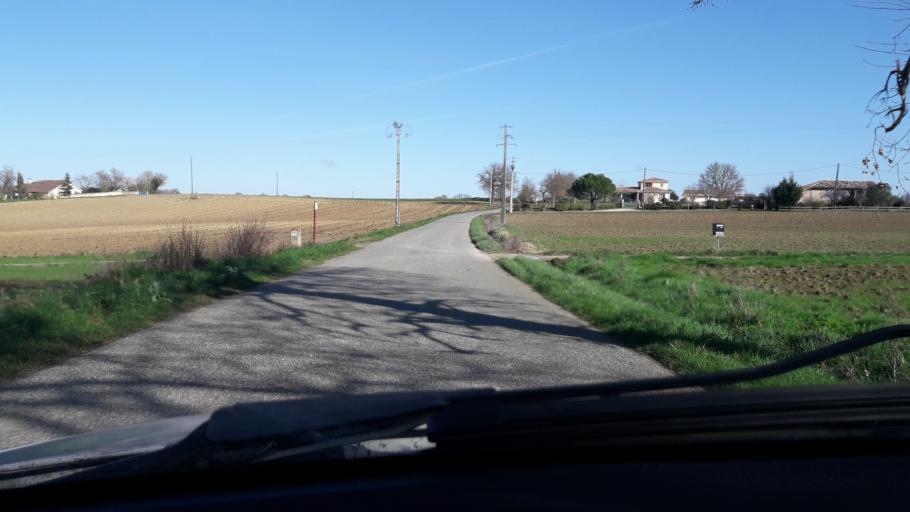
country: FR
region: Midi-Pyrenees
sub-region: Departement du Gers
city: Gimont
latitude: 43.6565
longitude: 1.0100
